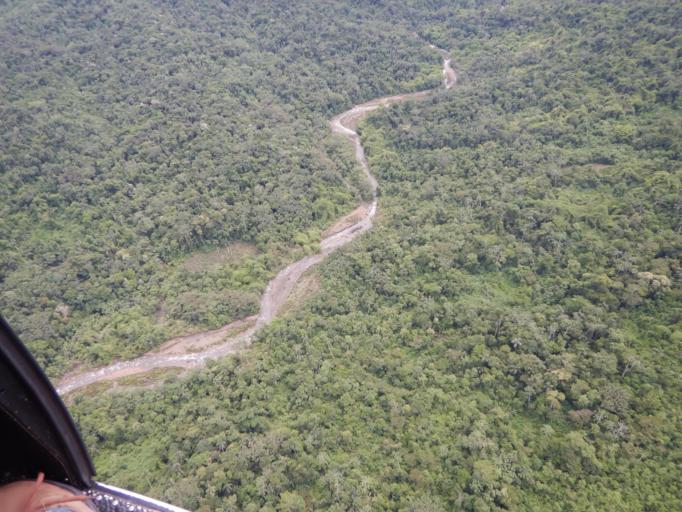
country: BO
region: Cochabamba
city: Totora
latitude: -17.3862
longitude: -65.0833
